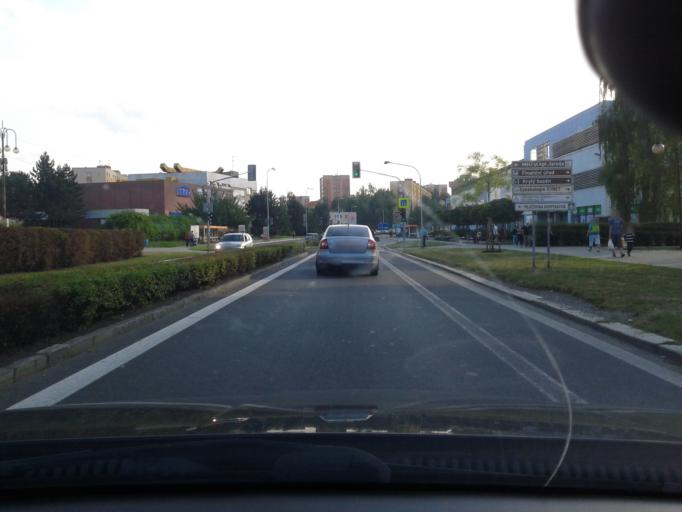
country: CZ
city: Dolni Lutyne
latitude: 49.8722
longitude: 18.4260
